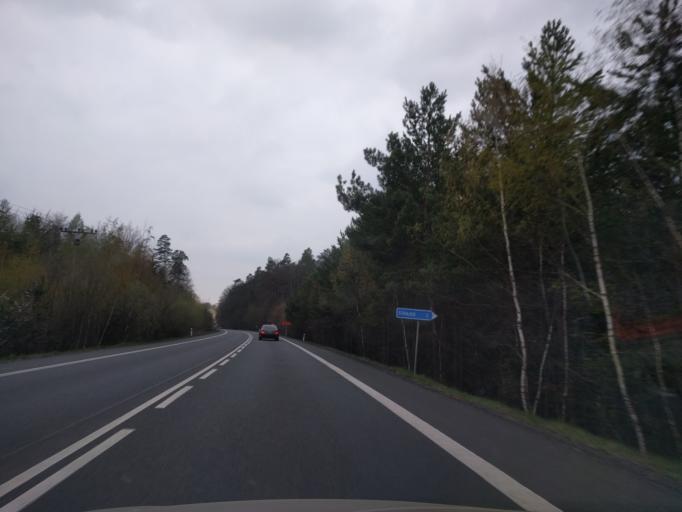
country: CZ
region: Central Bohemia
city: Kostelec nad Cernymi Lesy
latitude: 49.9912
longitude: 14.8034
